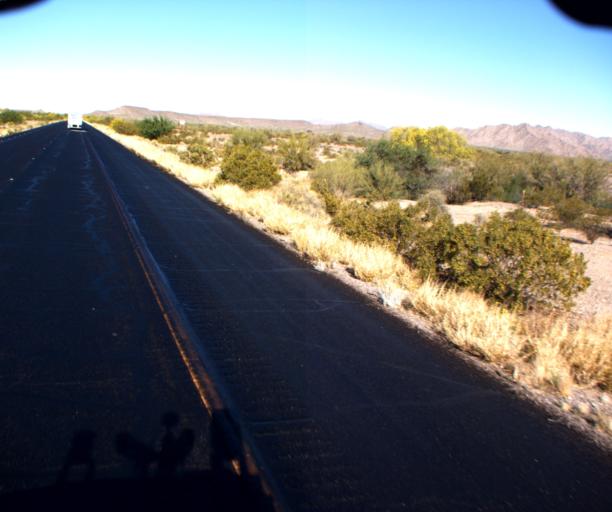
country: US
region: Arizona
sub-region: Pinal County
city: Maricopa
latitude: 32.8448
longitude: -112.2766
